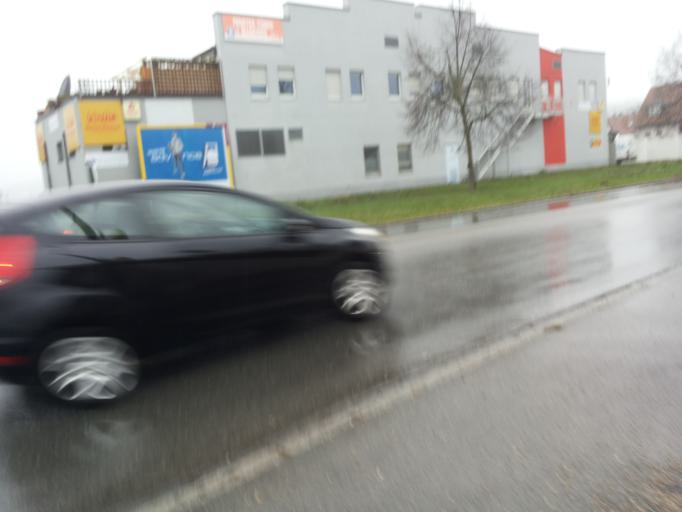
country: DE
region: Bavaria
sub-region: Regierungsbezirk Mittelfranken
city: Rosstal
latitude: 49.4261
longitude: 10.9066
